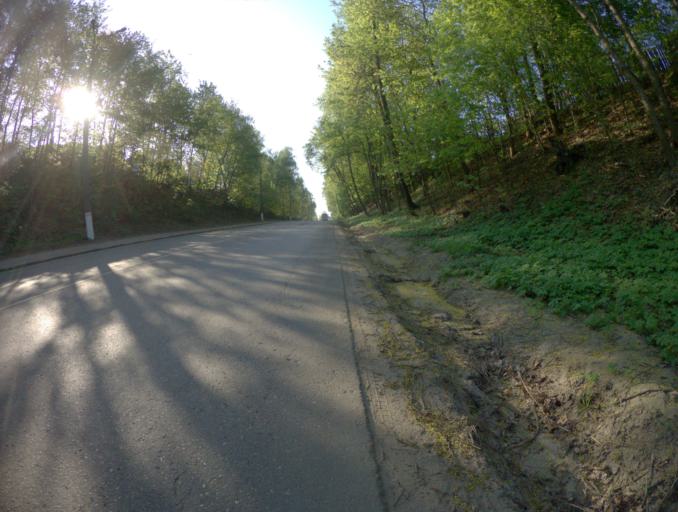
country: RU
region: Vladimir
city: Vyazniki
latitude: 56.2413
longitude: 42.1688
